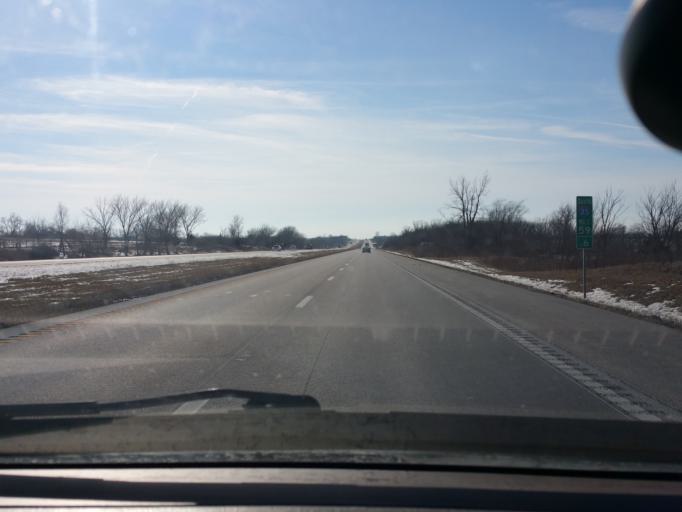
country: US
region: Missouri
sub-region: Clinton County
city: Cameron
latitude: 39.8281
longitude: -94.1884
